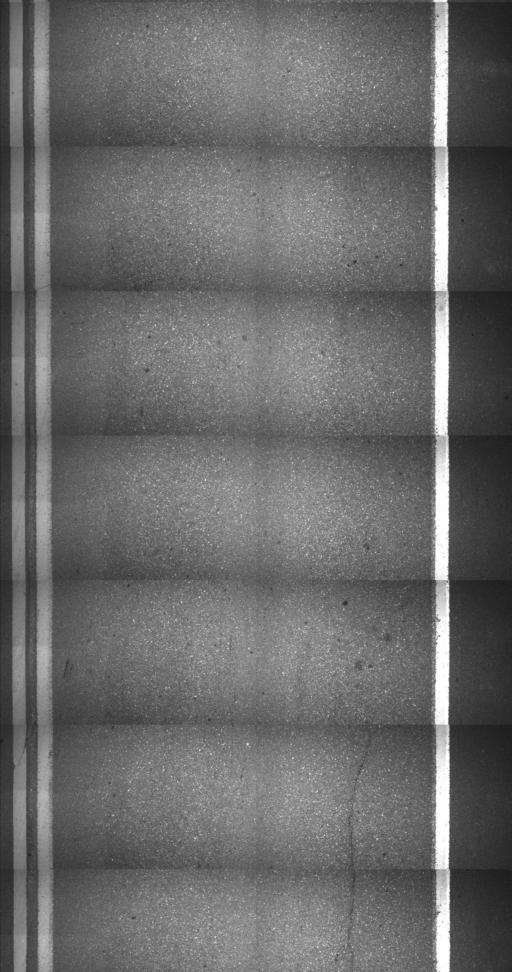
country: US
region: Vermont
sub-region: Caledonia County
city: Lyndon
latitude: 44.4933
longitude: -72.0050
